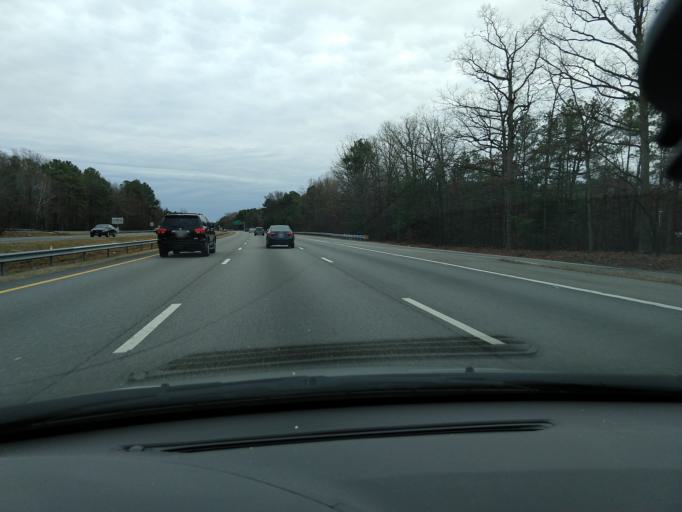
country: US
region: Virginia
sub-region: Henrico County
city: Chamberlayne
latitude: 37.6340
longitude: -77.4512
